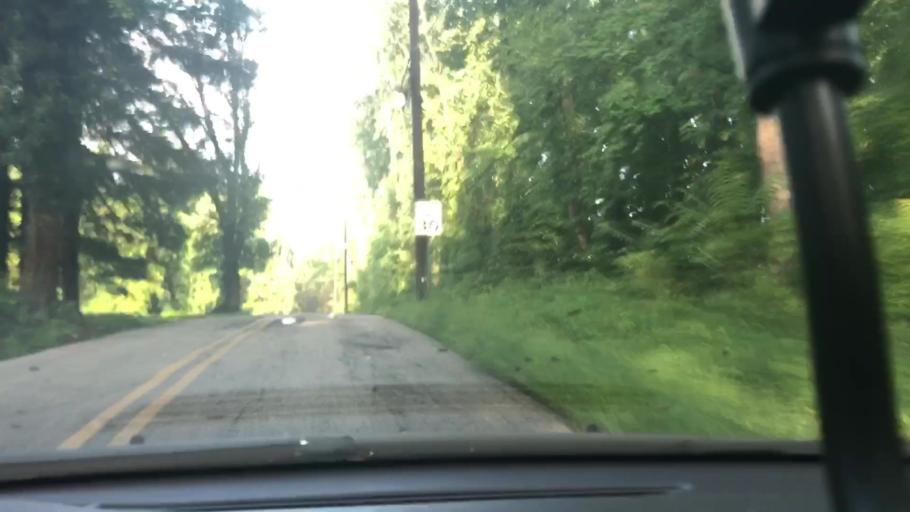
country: US
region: Pennsylvania
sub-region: Chester County
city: Kenilworth
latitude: 40.1803
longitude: -75.6457
